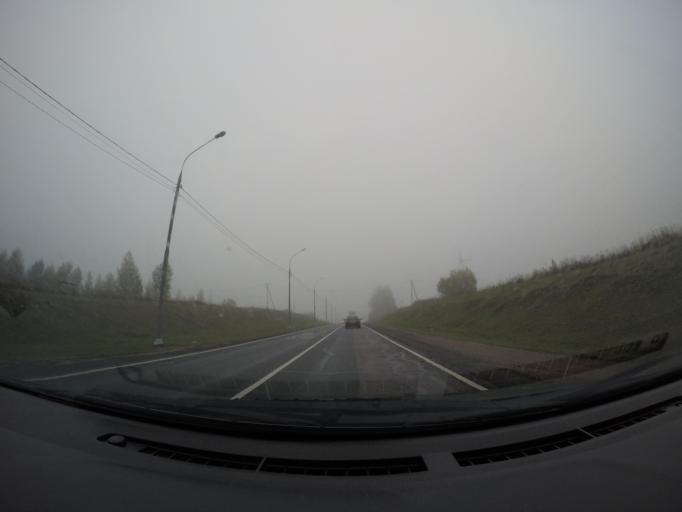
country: RU
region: Moskovskaya
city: Ruza
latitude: 55.7676
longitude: 36.2632
